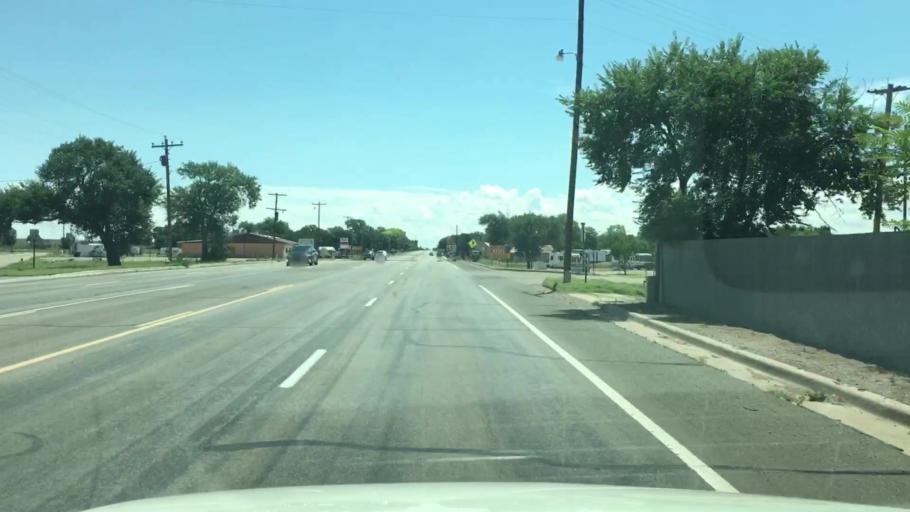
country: US
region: New Mexico
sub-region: De Baca County
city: Fort Sumner
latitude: 34.4676
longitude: -104.2327
